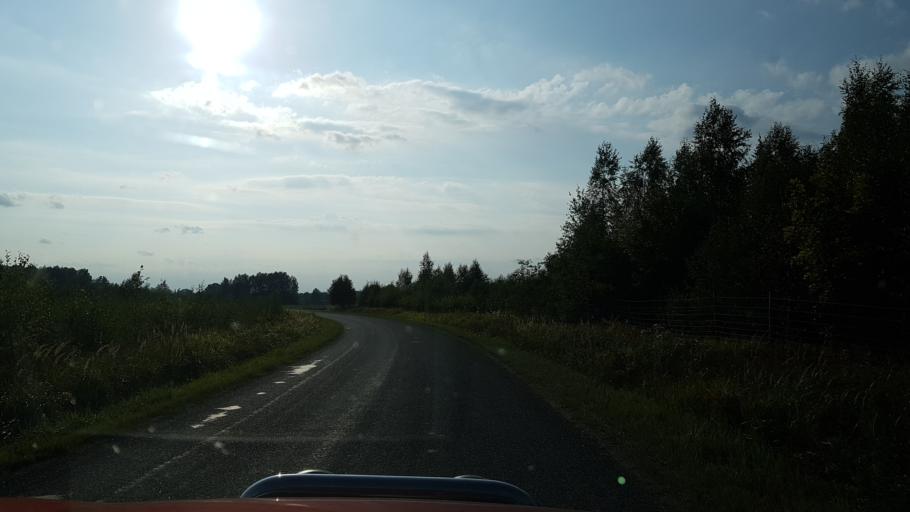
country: EE
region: Polvamaa
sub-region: Polva linn
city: Polva
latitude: 58.1259
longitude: 26.9740
